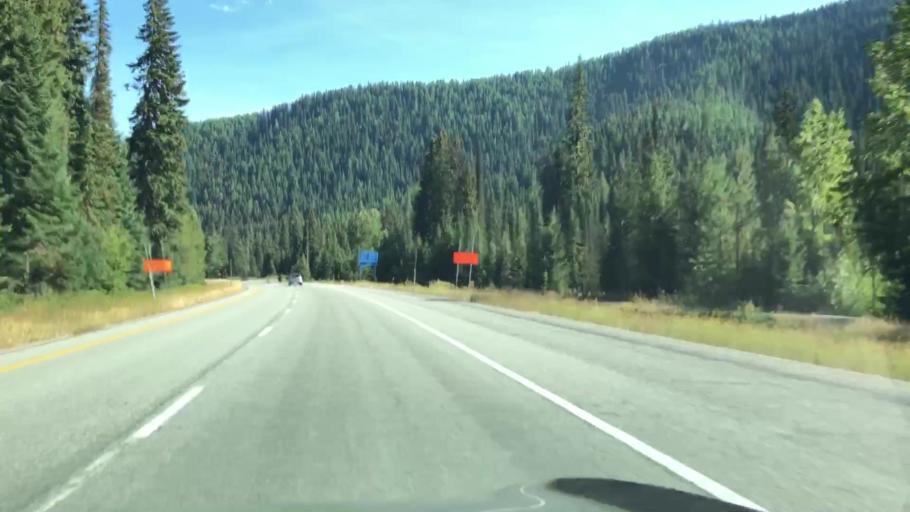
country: US
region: Idaho
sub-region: Shoshone County
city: Wallace
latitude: 47.4246
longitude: -115.6371
